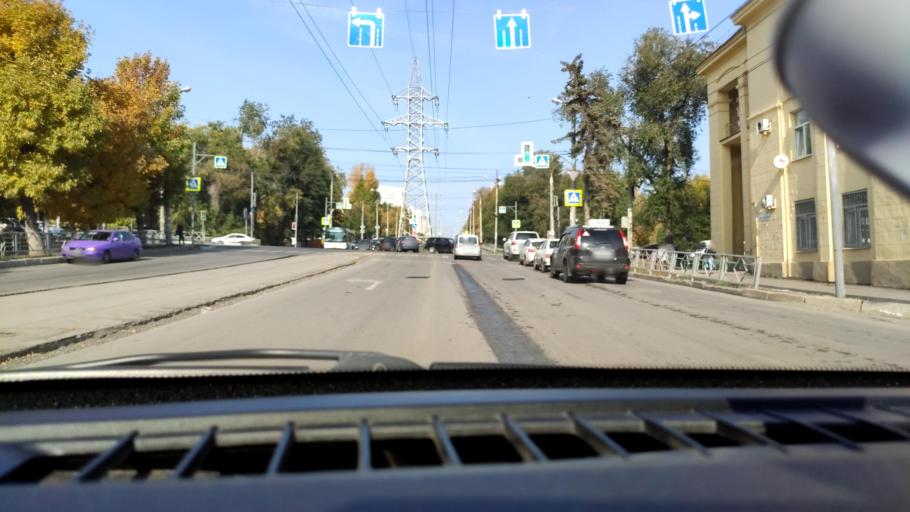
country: RU
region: Samara
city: Samara
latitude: 53.2007
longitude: 50.2141
